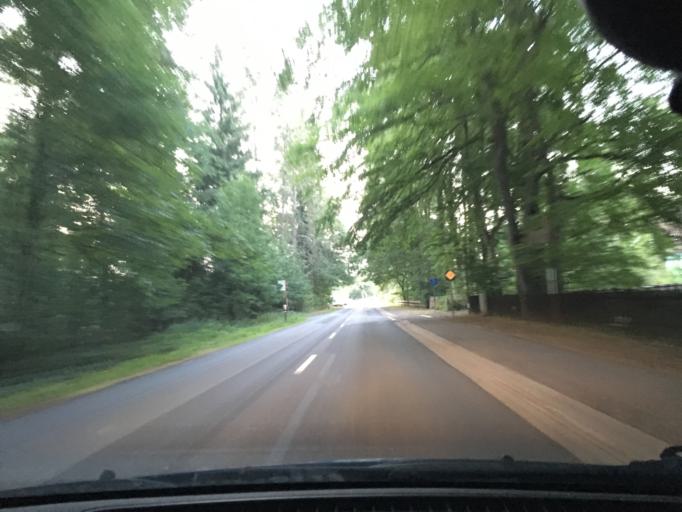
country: DE
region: Lower Saxony
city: Embsen
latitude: 53.1717
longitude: 10.3448
